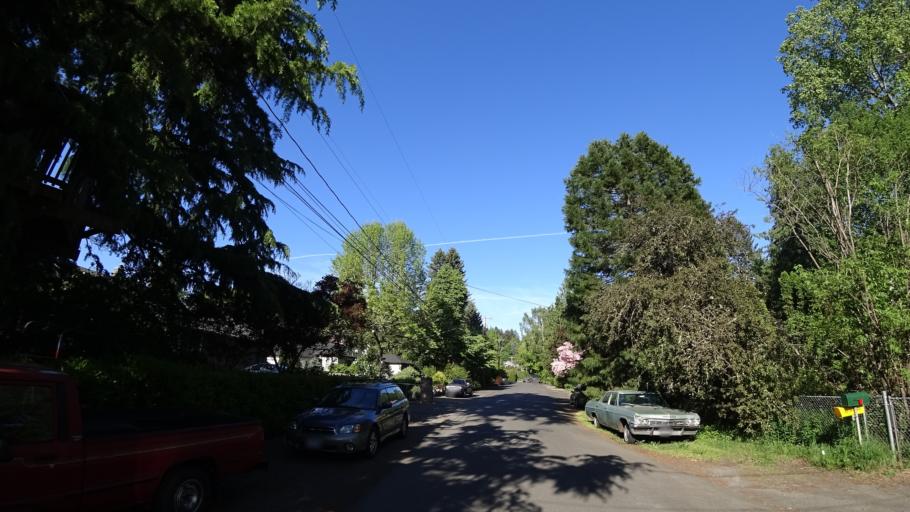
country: US
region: Oregon
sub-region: Washington County
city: West Slope
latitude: 45.4953
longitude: -122.7621
